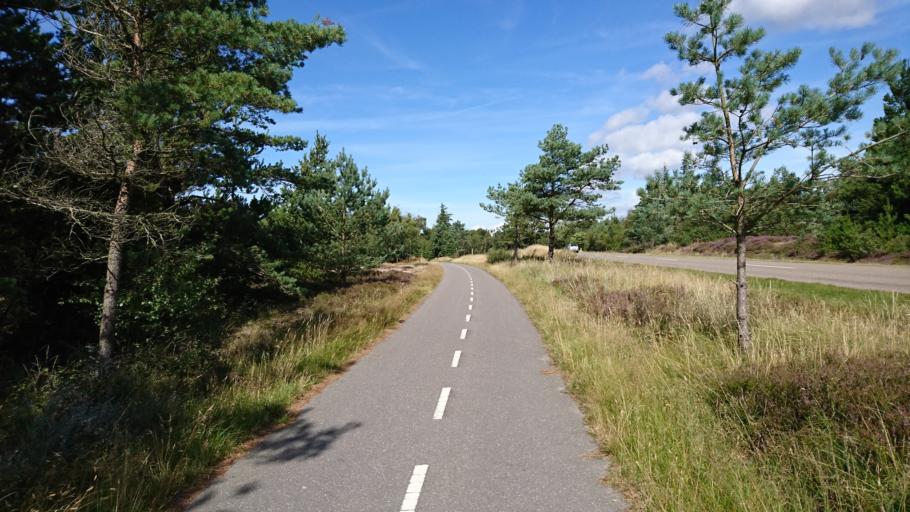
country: DK
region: South Denmark
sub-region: Fano Kommune
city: Nordby
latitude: 55.3952
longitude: 8.4236
